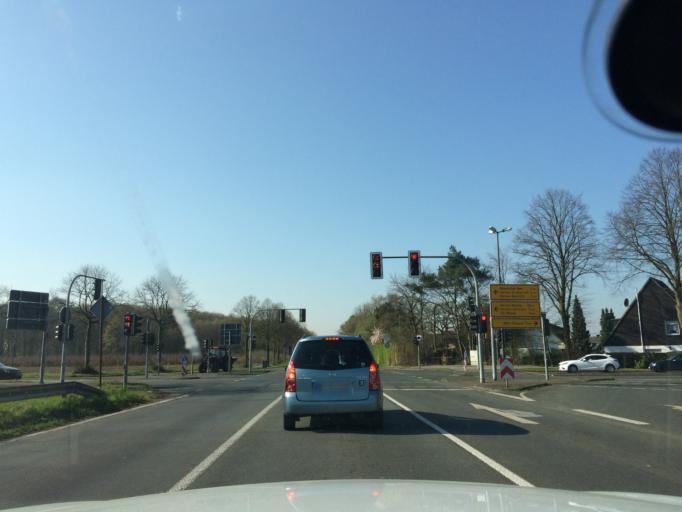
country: DE
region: North Rhine-Westphalia
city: Marl
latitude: 51.6168
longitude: 7.0828
